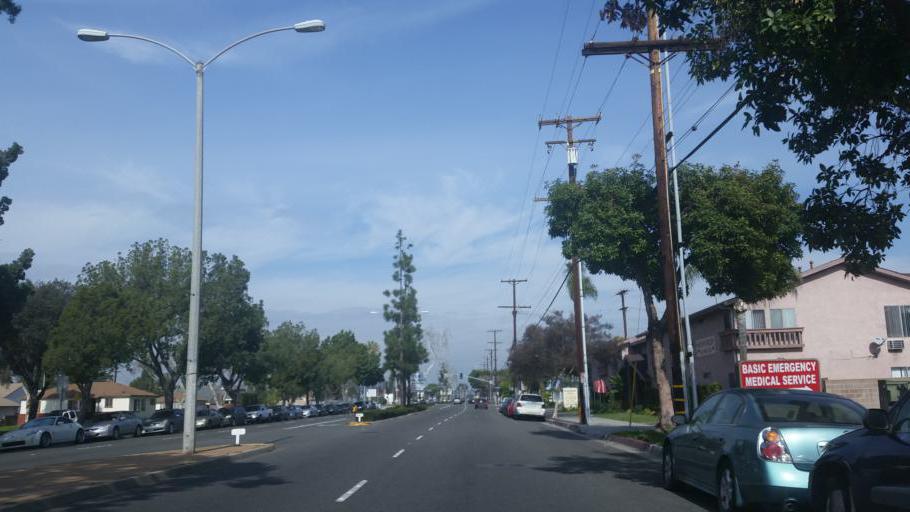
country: US
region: California
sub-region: Los Angeles County
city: Norwalk
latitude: 33.9127
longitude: -118.0992
